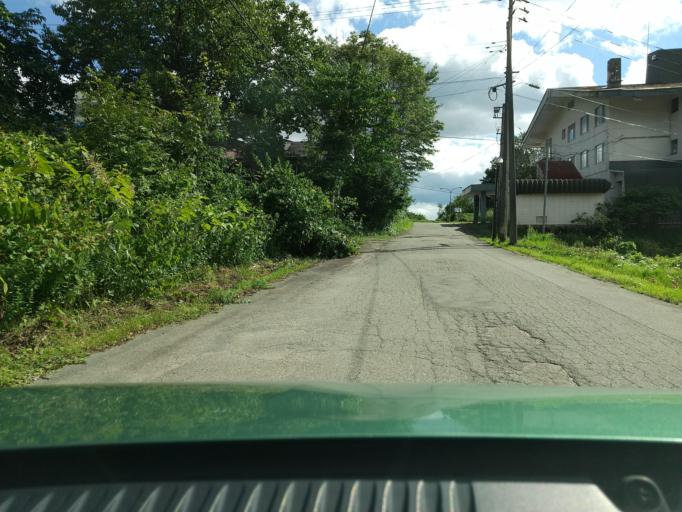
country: JP
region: Iwate
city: Shizukuishi
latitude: 39.7797
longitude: 140.7618
